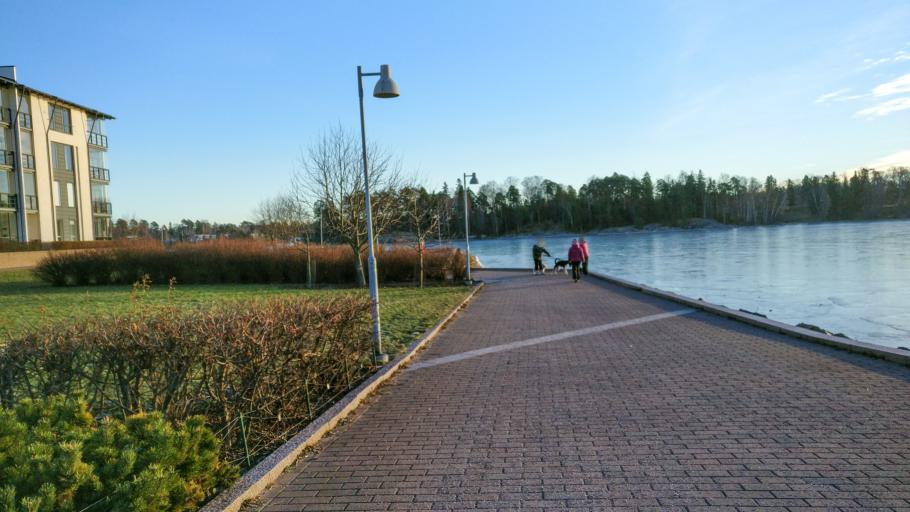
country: FI
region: Uusimaa
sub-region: Helsinki
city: Helsinki
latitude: 60.1848
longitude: 25.0299
